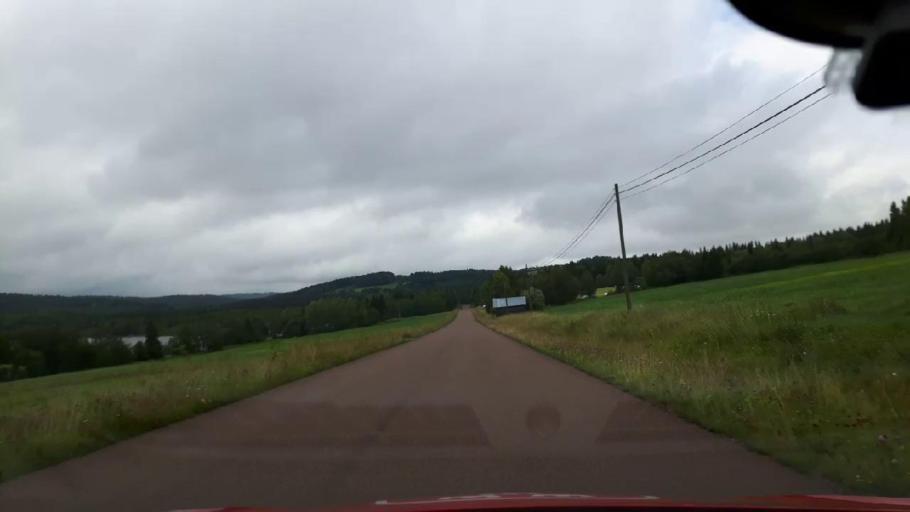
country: SE
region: Jaemtland
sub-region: Krokoms Kommun
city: Valla
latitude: 63.3887
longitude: 13.9024
